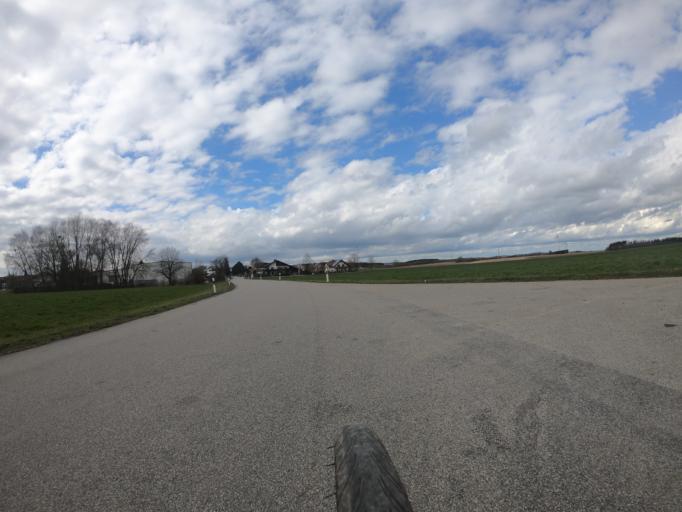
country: DE
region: Bavaria
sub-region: Upper Bavaria
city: Landsberied
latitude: 48.1785
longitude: 11.1955
